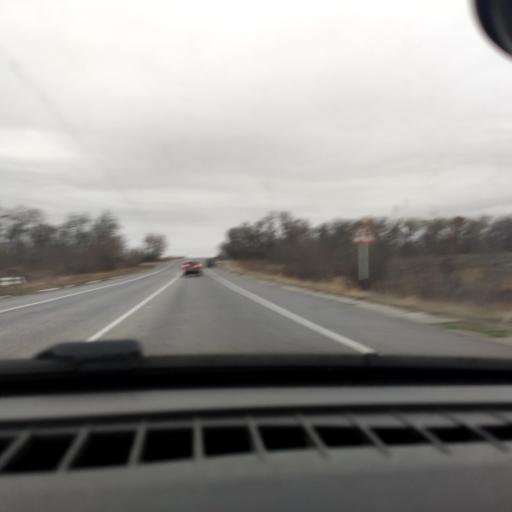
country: RU
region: Voronezj
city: Devitsa
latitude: 51.5730
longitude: 38.9748
